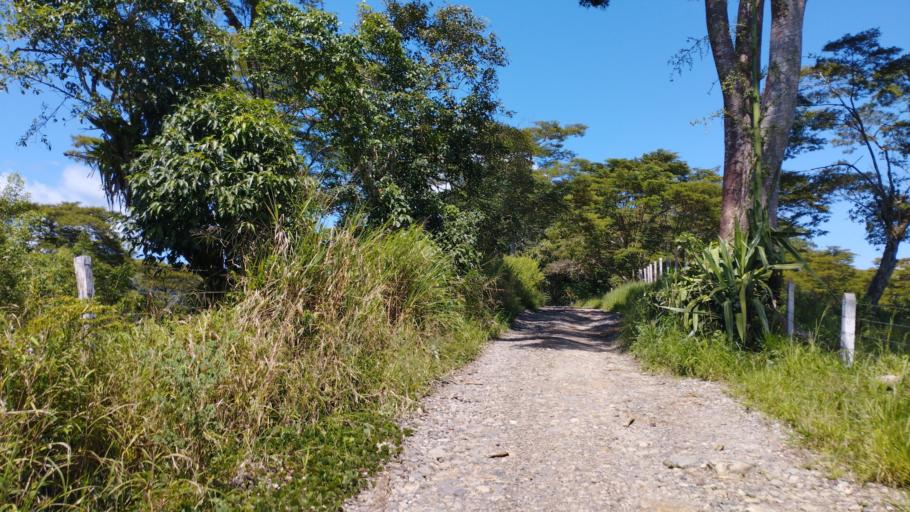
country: CO
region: Boyaca
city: San Luis de Gaceno
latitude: 4.7908
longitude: -73.1027
